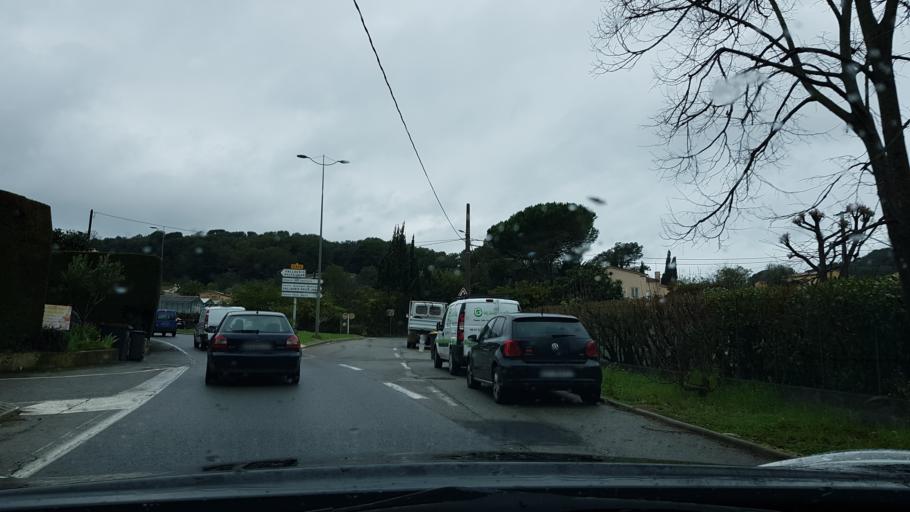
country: FR
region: Provence-Alpes-Cote d'Azur
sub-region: Departement des Alpes-Maritimes
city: Vallauris
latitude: 43.5897
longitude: 7.0559
